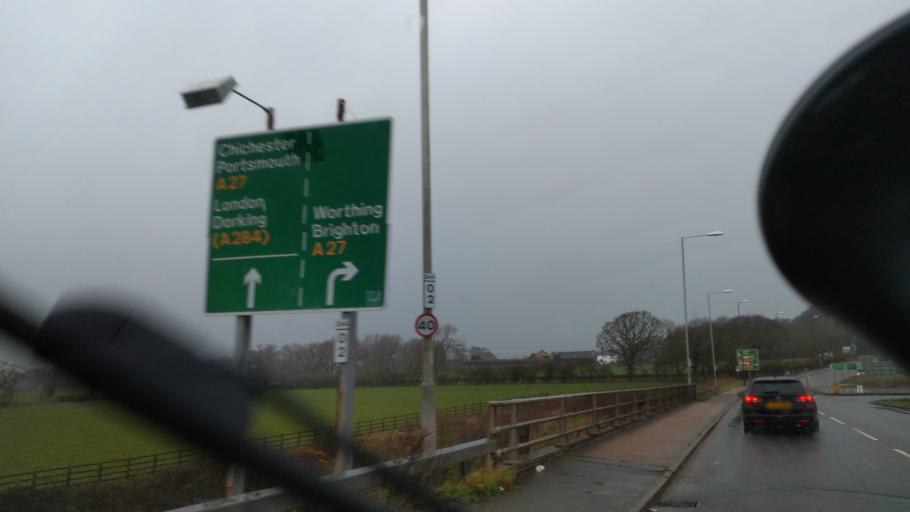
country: GB
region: England
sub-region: West Sussex
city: Arundel
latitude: 50.8434
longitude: -0.5407
